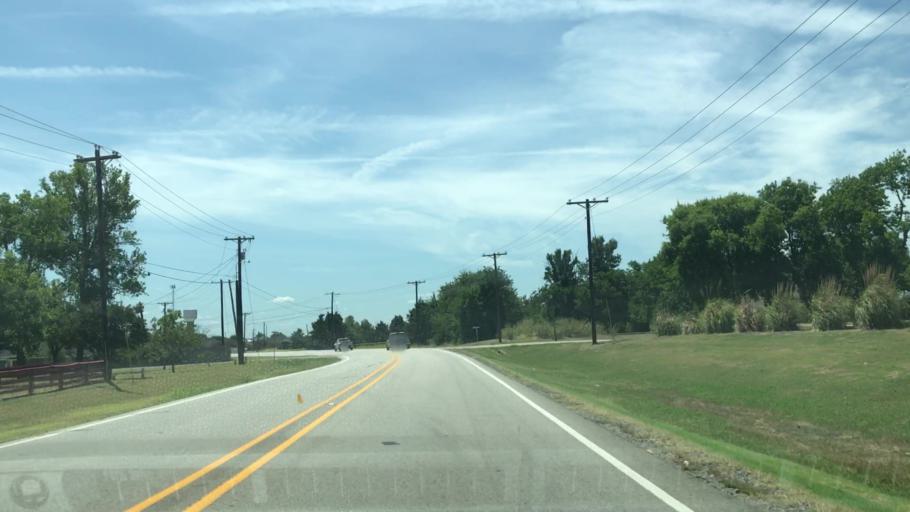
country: US
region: Texas
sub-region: Collin County
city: Saint Paul
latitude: 33.0370
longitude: -96.5504
